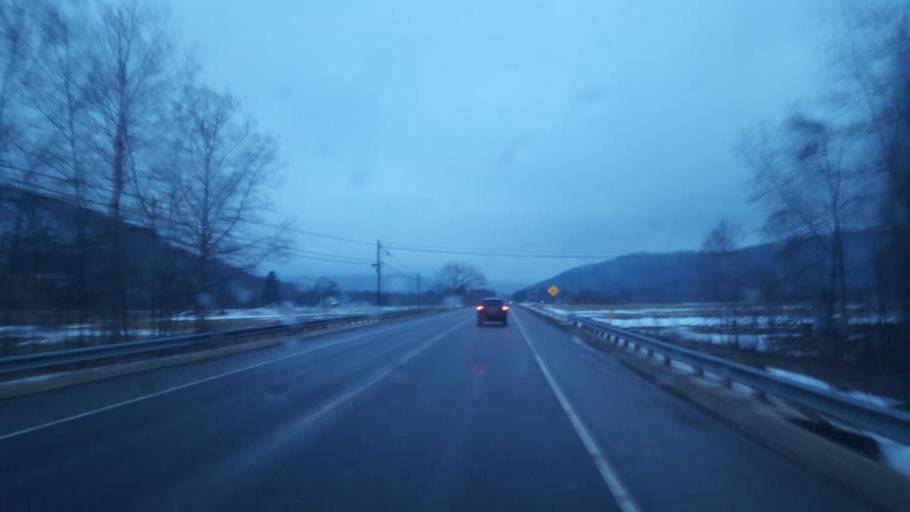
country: US
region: Pennsylvania
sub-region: McKean County
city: Port Allegany
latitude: 41.7920
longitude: -78.2434
